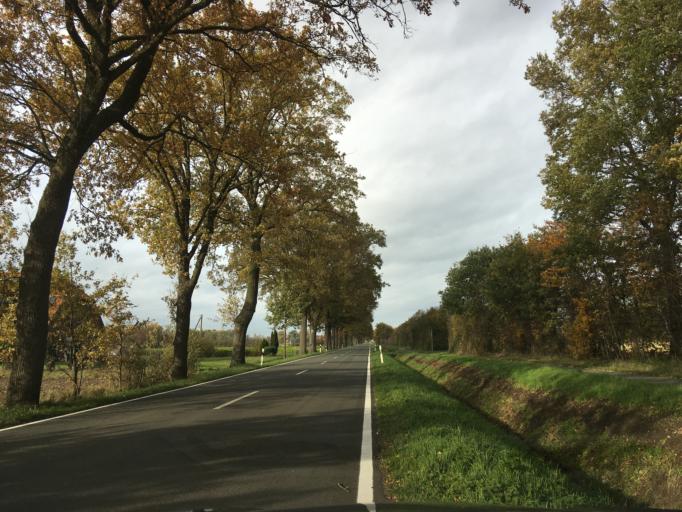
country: DE
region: North Rhine-Westphalia
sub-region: Regierungsbezirk Munster
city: Vreden
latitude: 52.0922
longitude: 6.8889
